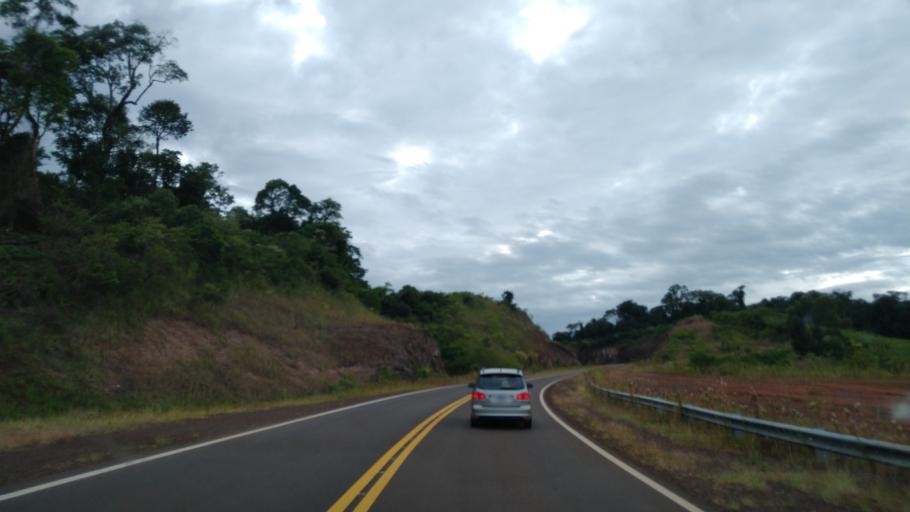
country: AR
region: Misiones
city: Bernardo de Irigoyen
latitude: -26.4528
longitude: -53.8616
